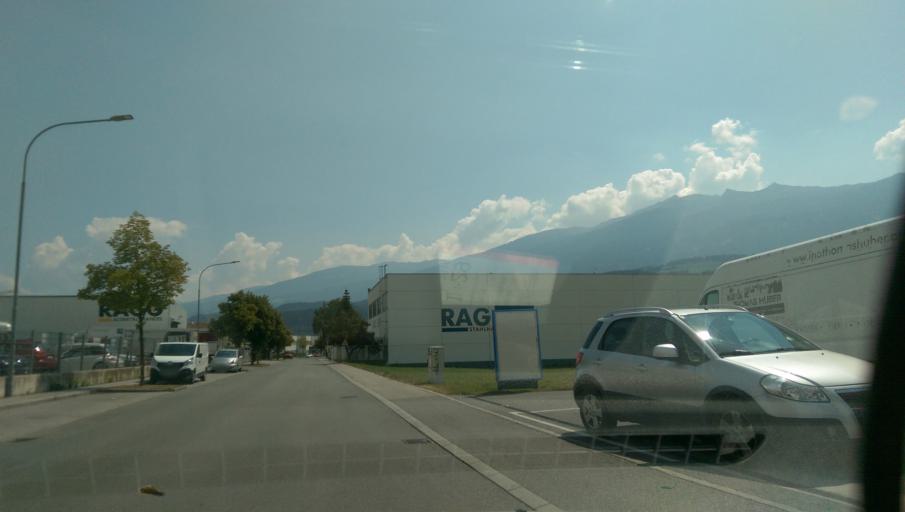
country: AT
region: Tyrol
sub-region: Politischer Bezirk Innsbruck Land
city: Ampass
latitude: 47.2680
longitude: 11.4327
